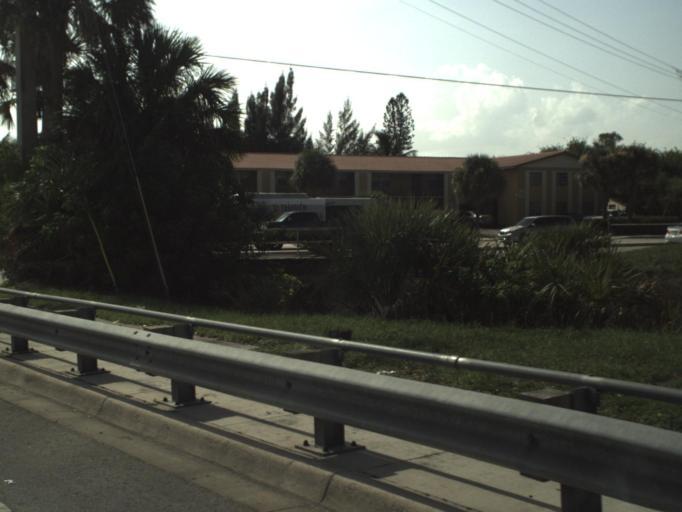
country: US
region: Florida
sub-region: Broward County
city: Coral Springs
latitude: 26.2723
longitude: -80.2344
